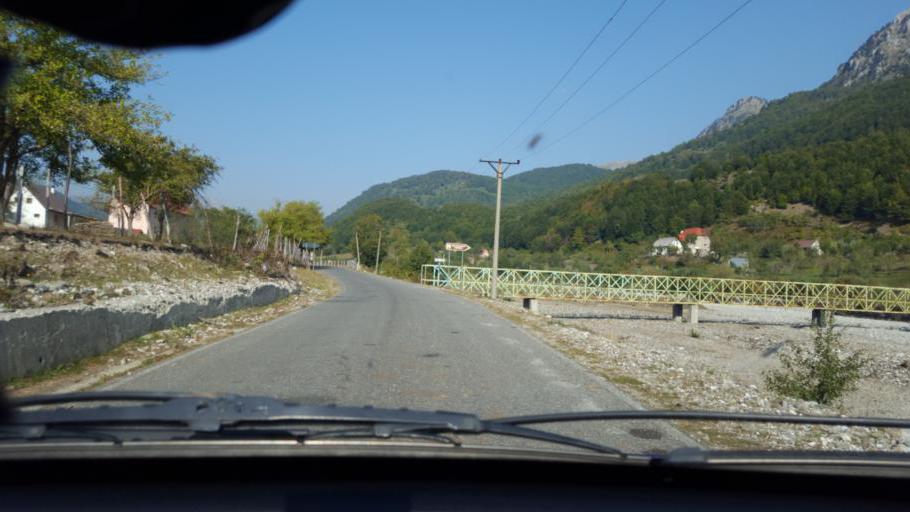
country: ME
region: Andrijevica
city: Andrijevica
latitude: 42.5870
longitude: 19.7171
